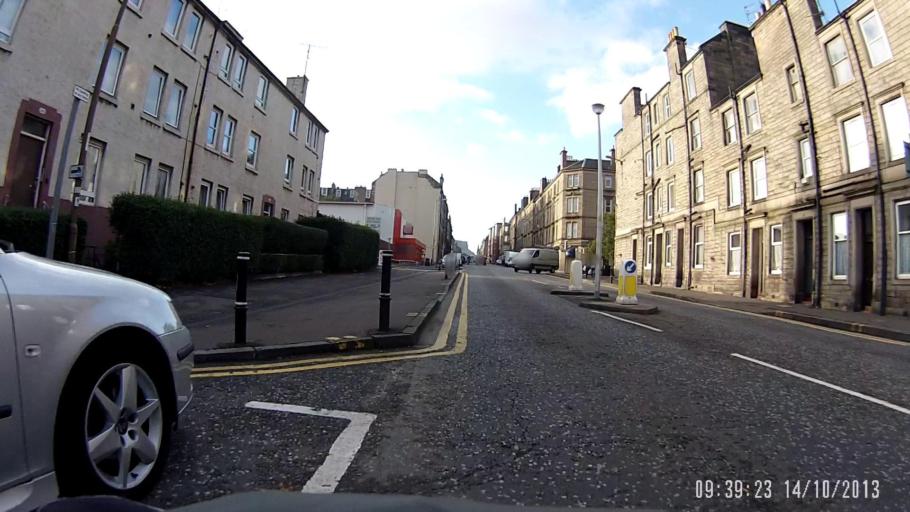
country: GB
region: Scotland
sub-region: West Lothian
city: Seafield
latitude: 55.9637
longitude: -3.1706
